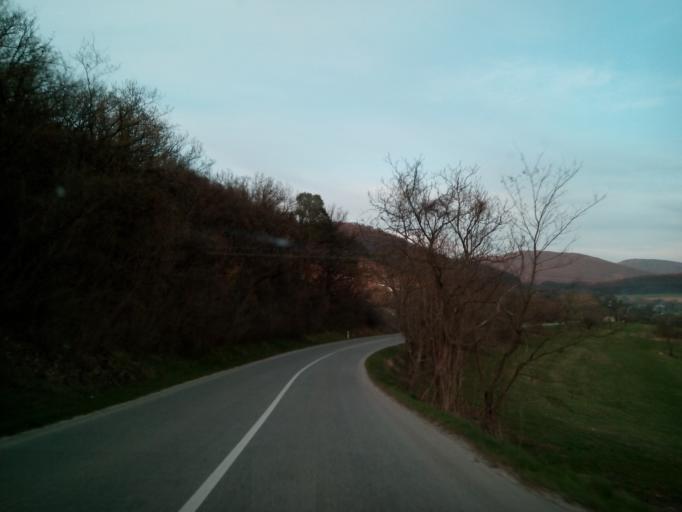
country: SK
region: Kosicky
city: Roznava
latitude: 48.6649
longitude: 20.3932
